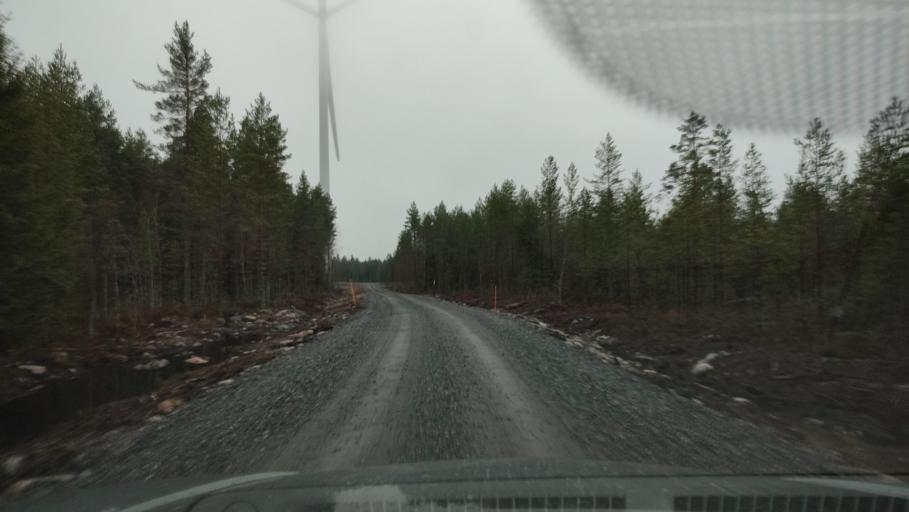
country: FI
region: Southern Ostrobothnia
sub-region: Suupohja
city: Karijoki
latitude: 62.1474
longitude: 21.6133
